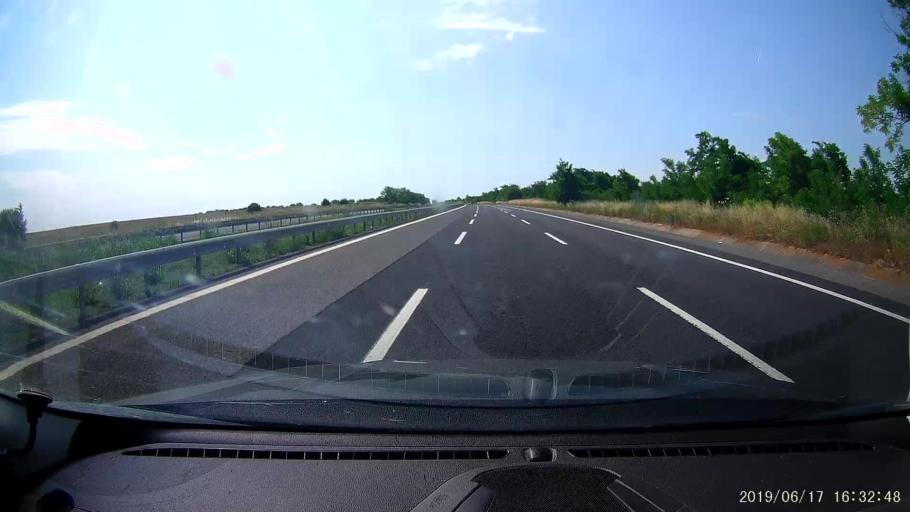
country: TR
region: Kirklareli
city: Buyukkaristiran
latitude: 41.3741
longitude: 27.5911
